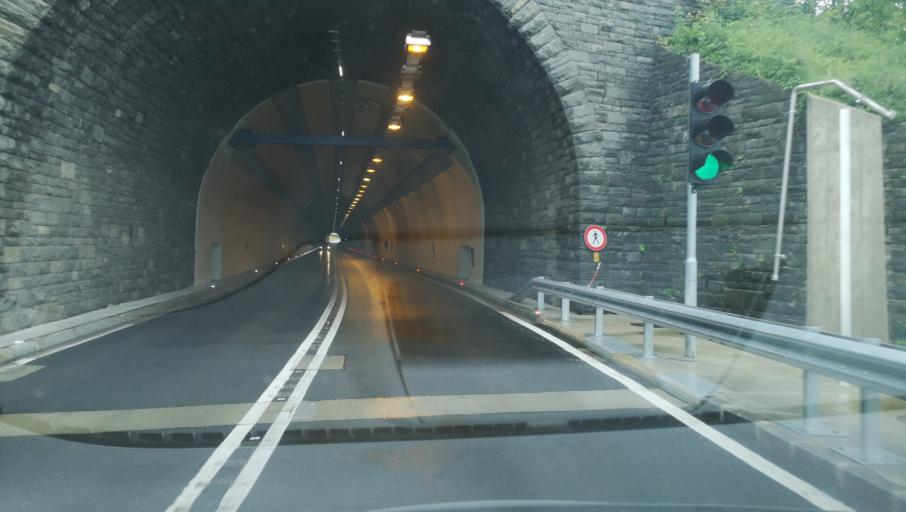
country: AT
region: Lower Austria
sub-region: Politischer Bezirk Krems
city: Durnstein
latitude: 48.3973
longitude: 15.5189
